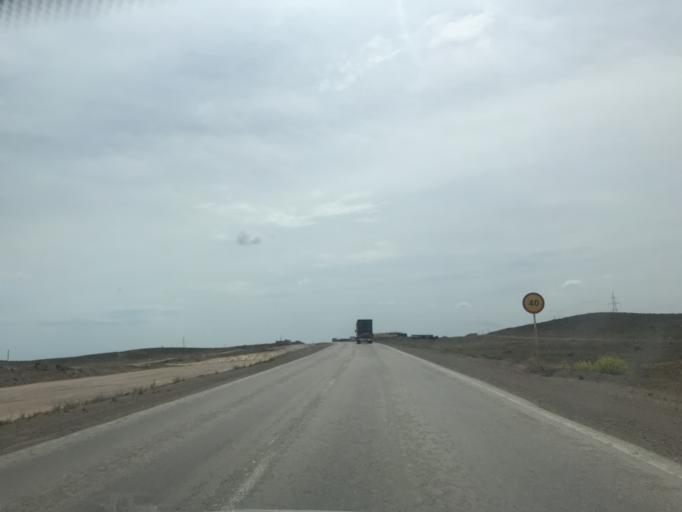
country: KZ
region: Zhambyl
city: Mynaral
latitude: 45.3459
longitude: 73.6944
